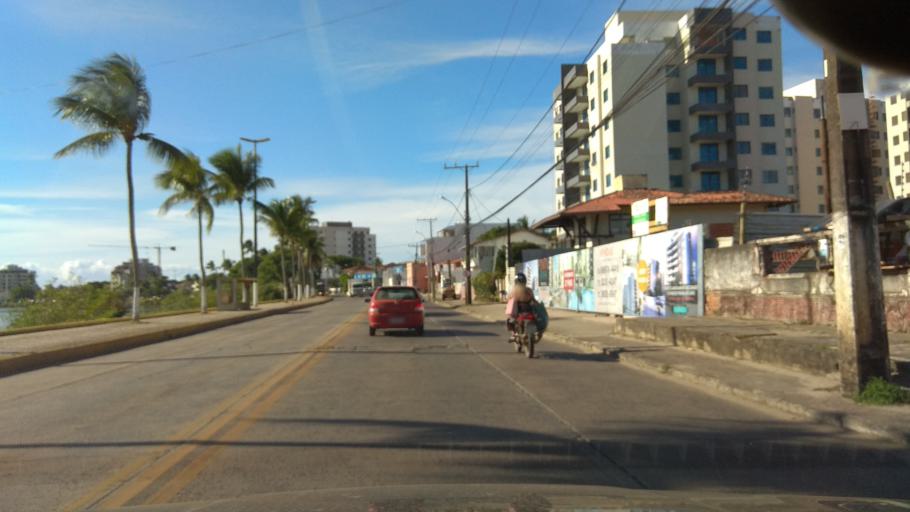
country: BR
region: Bahia
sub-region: Ilheus
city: Ilheus
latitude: -14.8102
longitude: -39.0347
